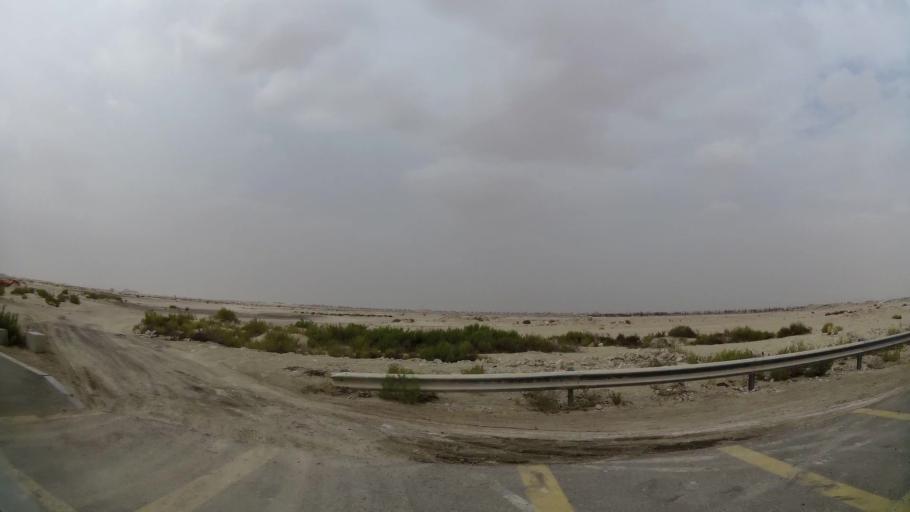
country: AE
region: Abu Dhabi
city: Abu Dhabi
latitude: 24.3873
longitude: 54.6798
